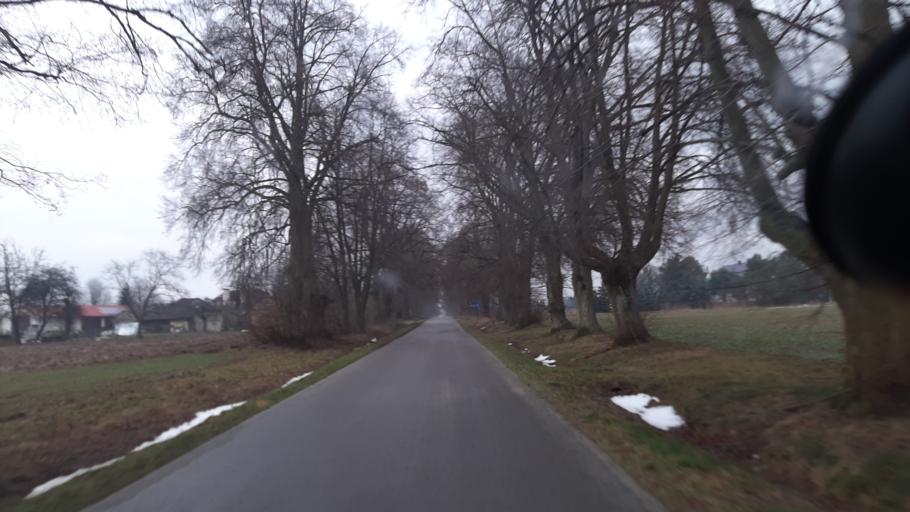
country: PL
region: Lublin Voivodeship
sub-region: Powiat lubelski
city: Lublin
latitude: 51.3419
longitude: 22.5328
